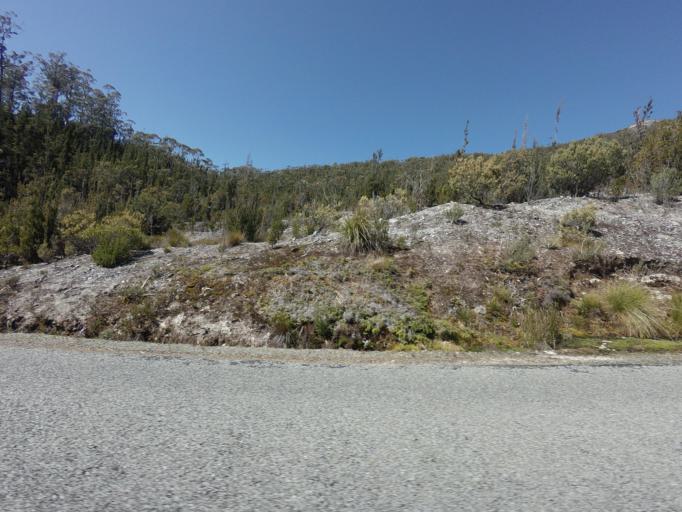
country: AU
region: Tasmania
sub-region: Huon Valley
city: Geeveston
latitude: -42.8026
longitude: 146.3945
